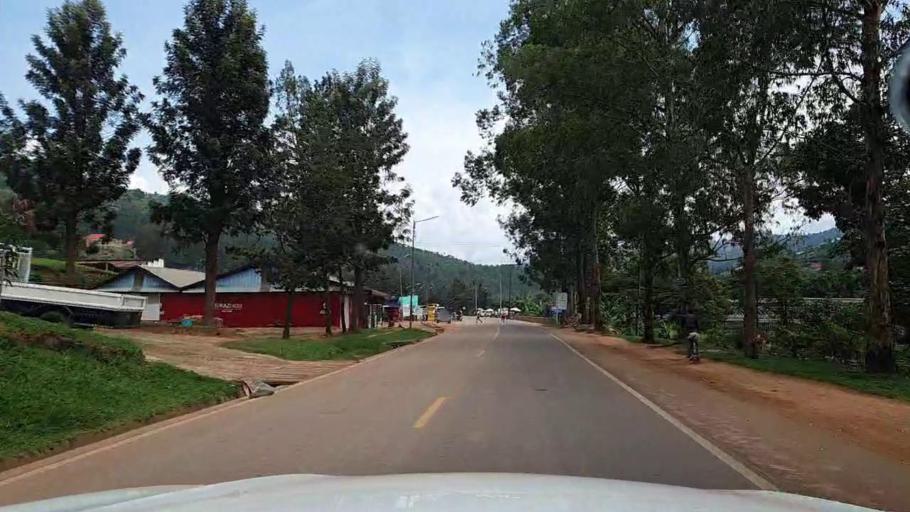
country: RW
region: Kigali
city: Kigali
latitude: -1.8679
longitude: 30.0862
